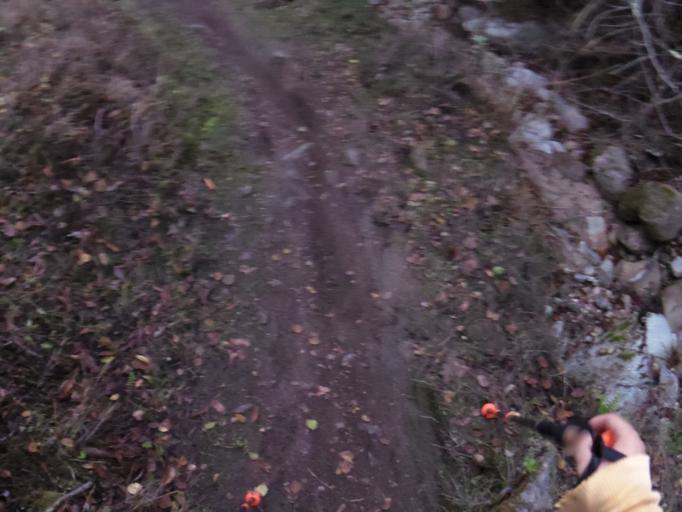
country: US
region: California
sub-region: Monterey County
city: Salinas
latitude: 36.5767
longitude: -121.6850
